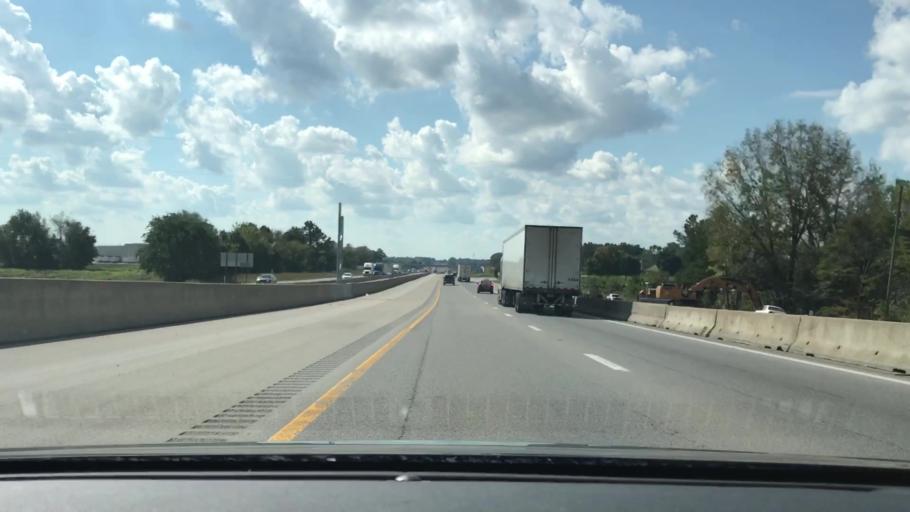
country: US
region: Tennessee
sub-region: Sumner County
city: Portland
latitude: 36.6401
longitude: -86.5710
